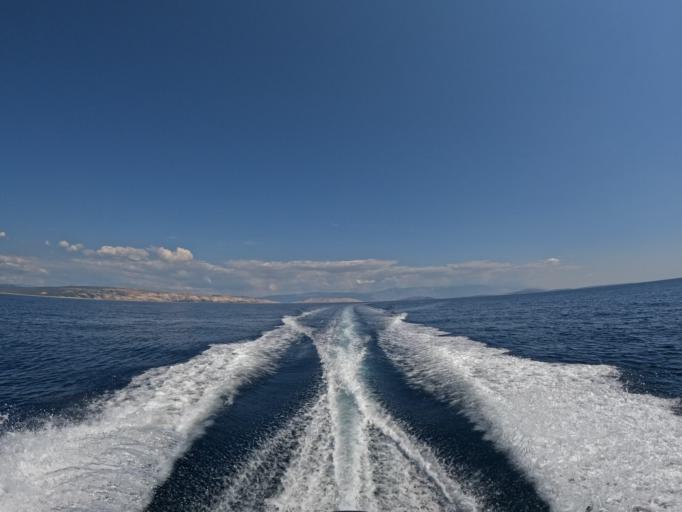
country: HR
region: Primorsko-Goranska
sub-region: Grad Krk
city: Krk
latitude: 44.9249
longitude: 14.5443
